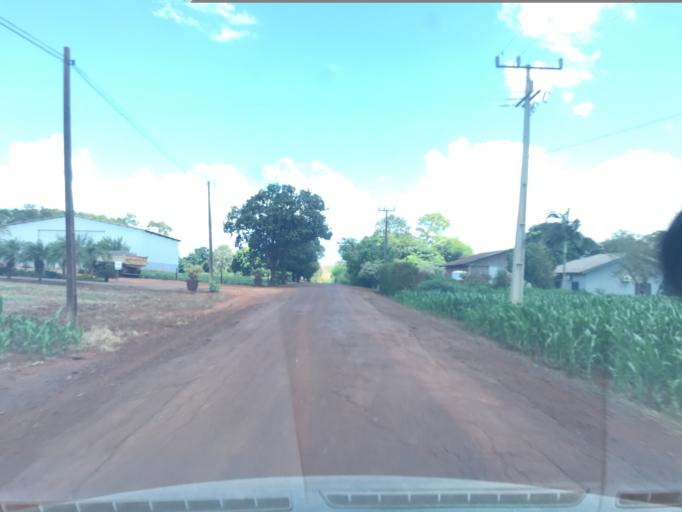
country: BR
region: Parana
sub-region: Palotina
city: Palotina
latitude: -24.2951
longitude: -53.8586
